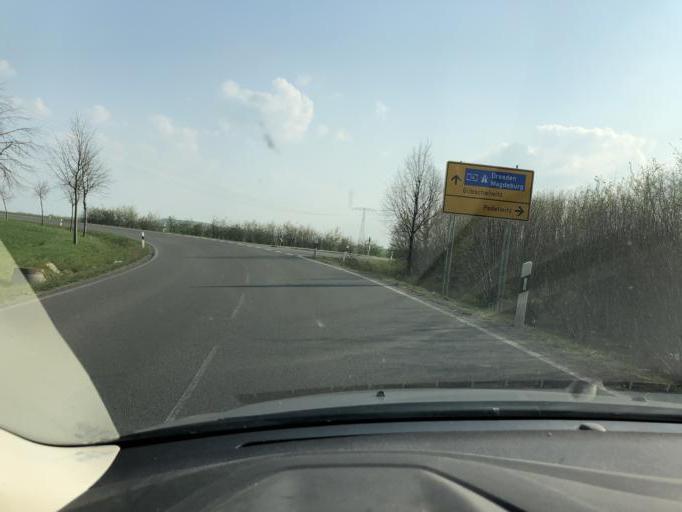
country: DE
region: Saxony
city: Rackwitz
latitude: 51.4308
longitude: 12.3863
